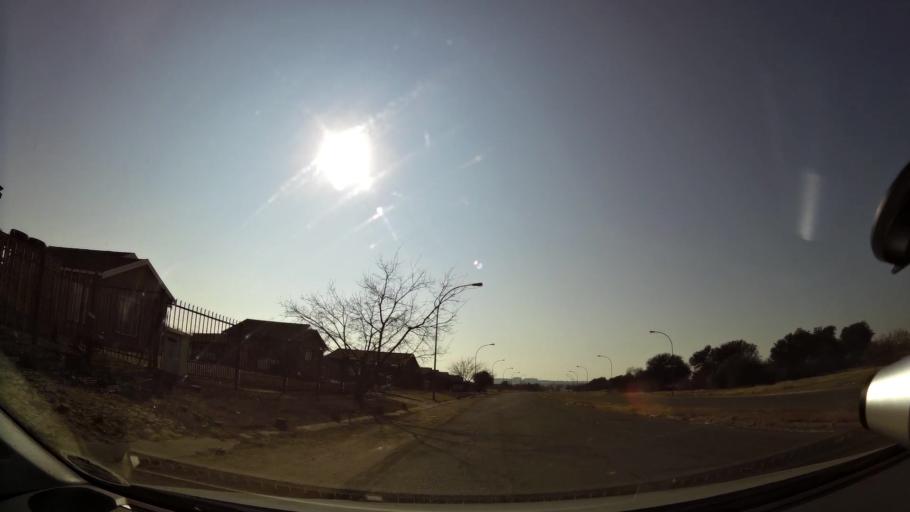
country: ZA
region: Orange Free State
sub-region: Mangaung Metropolitan Municipality
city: Bloemfontein
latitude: -29.1867
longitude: 26.1754
